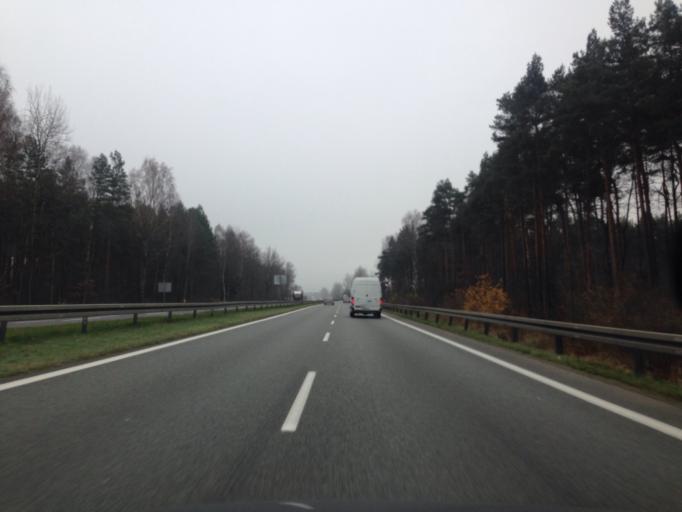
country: PL
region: Silesian Voivodeship
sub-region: Powiat bedzinski
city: Siewierz
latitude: 50.5199
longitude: 19.1934
